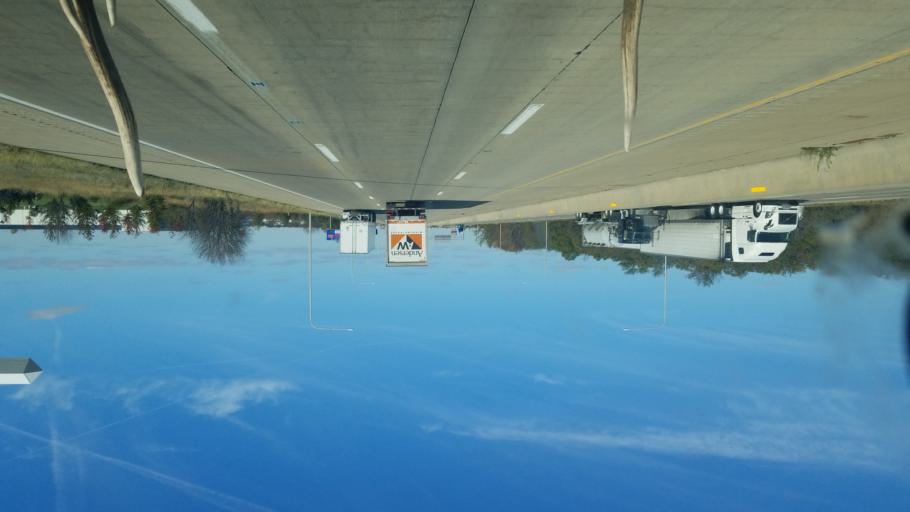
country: US
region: Illinois
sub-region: Effingham County
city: Effingham
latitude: 39.1060
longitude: -88.5731
